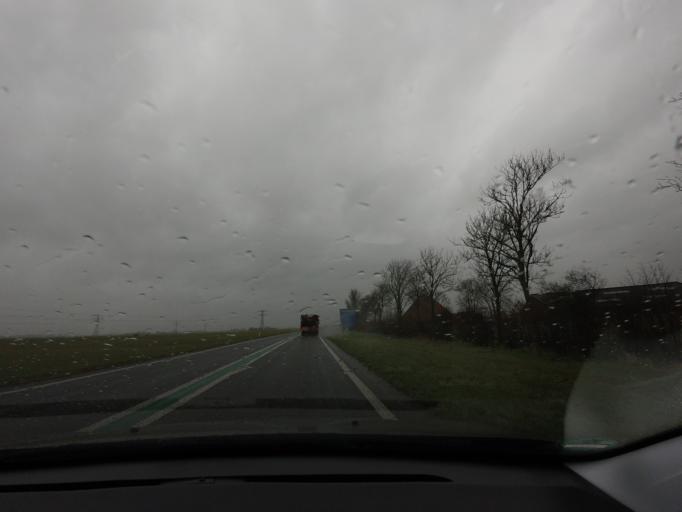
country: NL
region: Friesland
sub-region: Sudwest Fryslan
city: Bolsward
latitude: 53.0726
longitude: 5.5106
